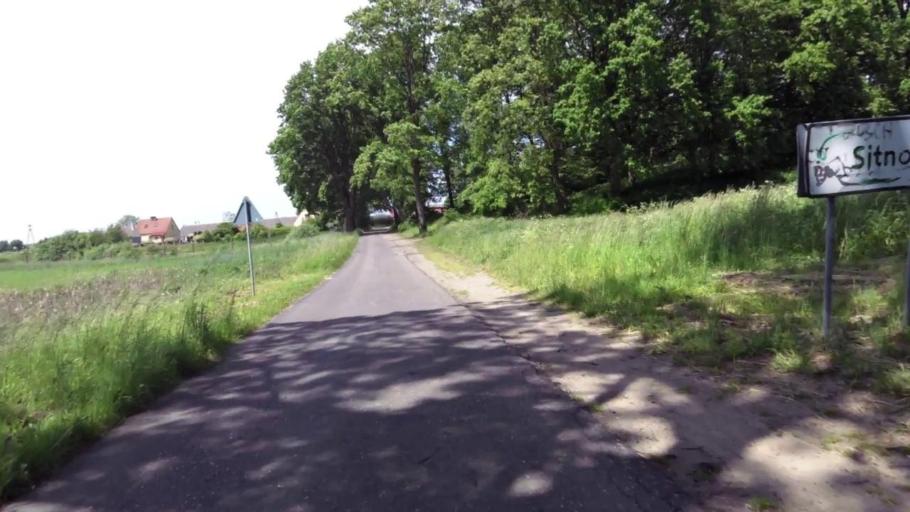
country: PL
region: West Pomeranian Voivodeship
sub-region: Powiat szczecinecki
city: Szczecinek
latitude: 53.6565
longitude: 16.6706
